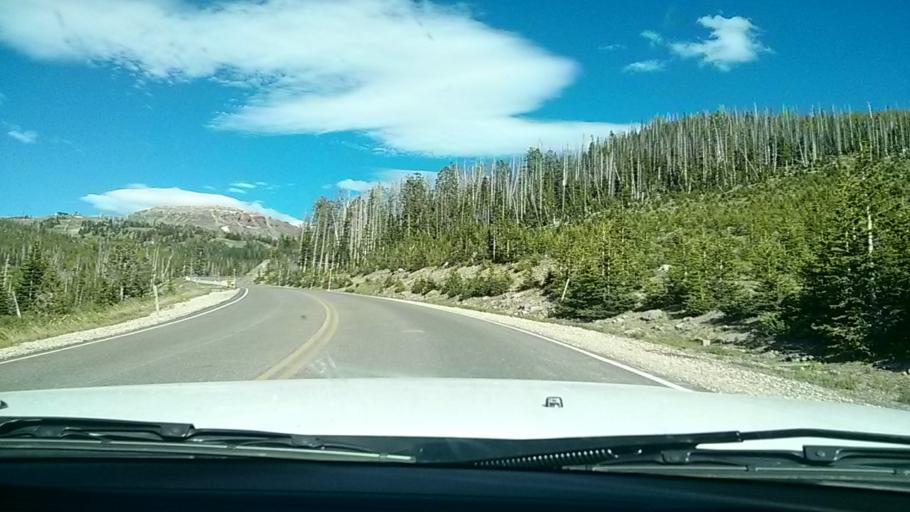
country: US
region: Utah
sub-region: Iron County
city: Parowan
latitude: 37.6813
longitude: -112.8553
